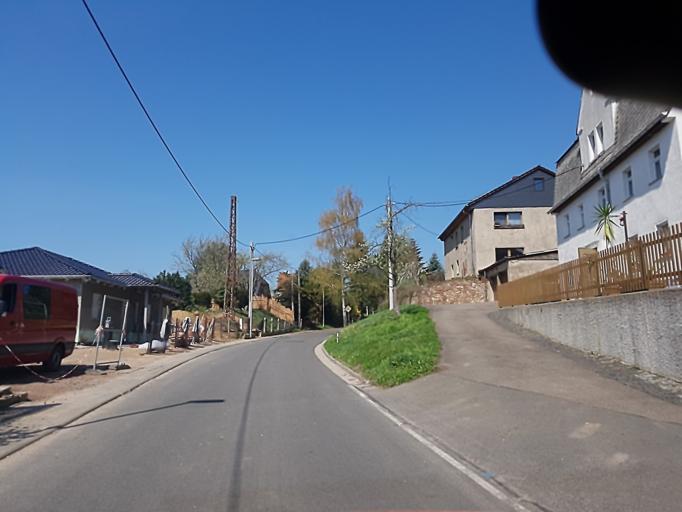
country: DE
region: Saxony
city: Bockelwitz
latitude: 51.1678
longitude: 12.9805
